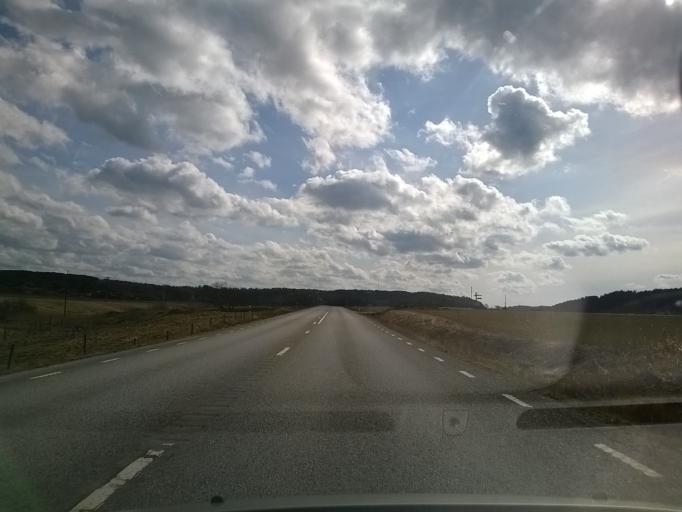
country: SE
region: Vaestra Goetaland
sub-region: Orust
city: Henan
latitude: 58.1690
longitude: 11.7015
